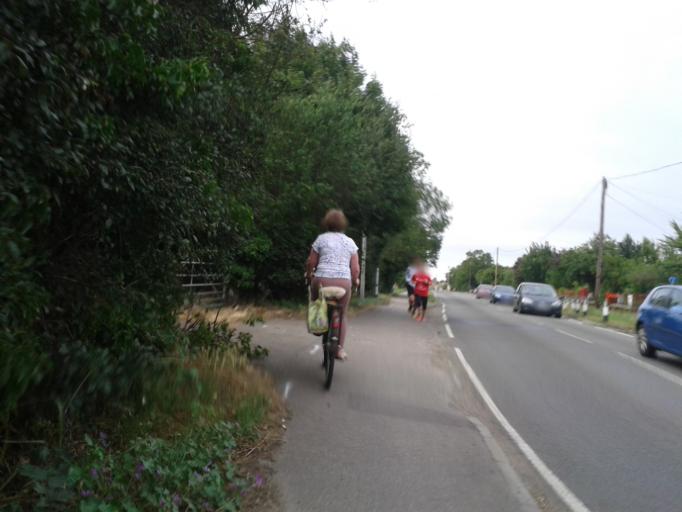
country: GB
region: England
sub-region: Cambridgeshire
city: Waterbeach
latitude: 52.2219
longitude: 0.1742
